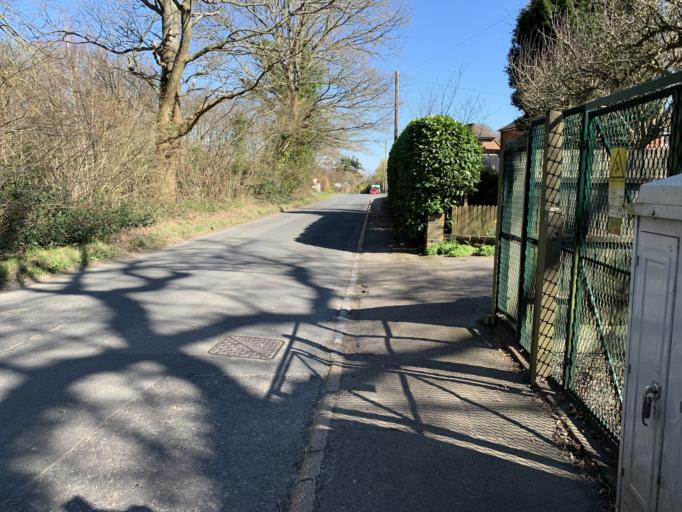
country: GB
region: England
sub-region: East Sussex
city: Uckfield
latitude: 50.9820
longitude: 0.0993
